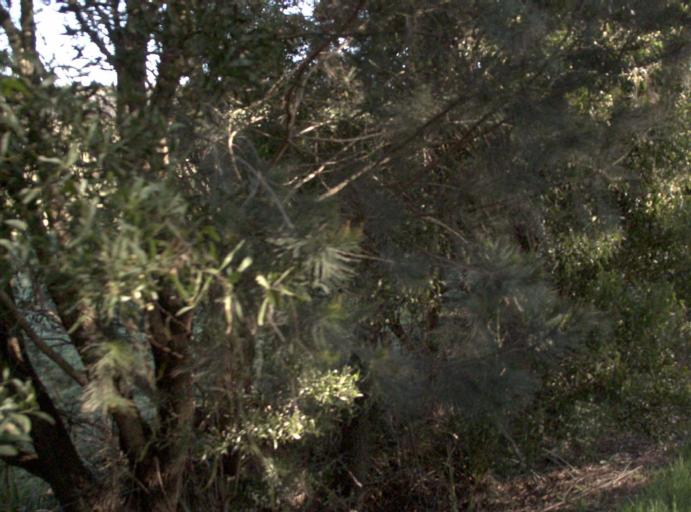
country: AU
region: Tasmania
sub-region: Dorset
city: Bridport
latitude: -41.1041
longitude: 147.1980
